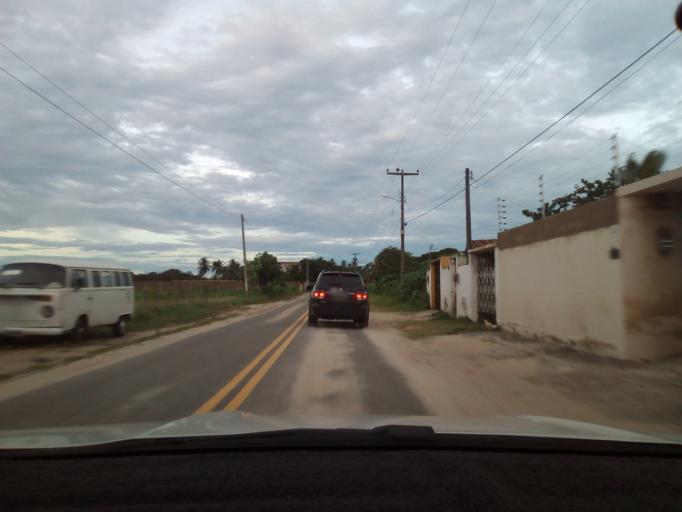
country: BR
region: Ceara
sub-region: Beberibe
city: Beberibe
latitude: -4.1851
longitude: -38.1245
